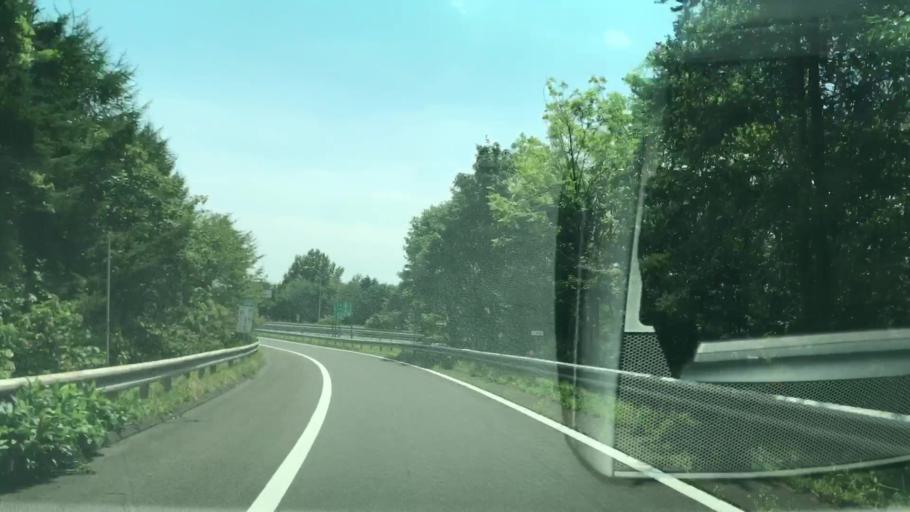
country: JP
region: Hokkaido
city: Muroran
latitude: 42.3989
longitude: 141.0813
